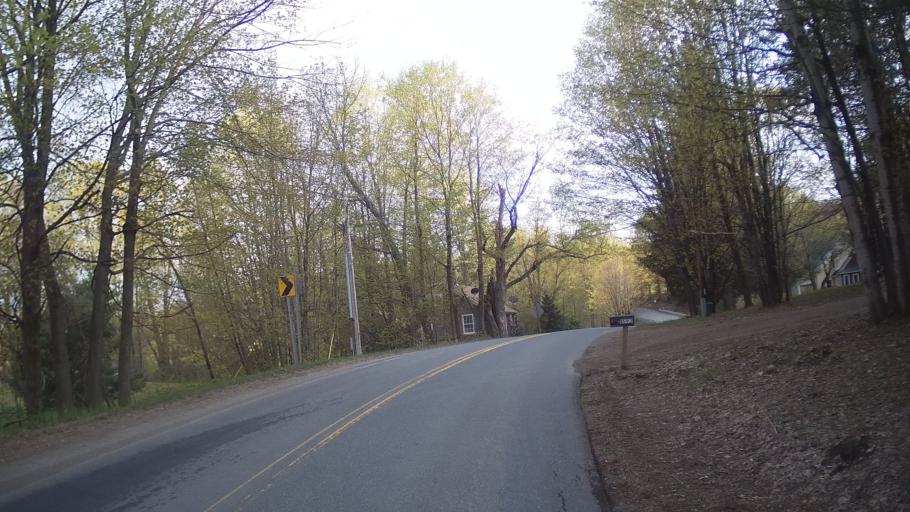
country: US
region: Vermont
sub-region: Orleans County
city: Newport
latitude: 44.9114
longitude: -72.4309
